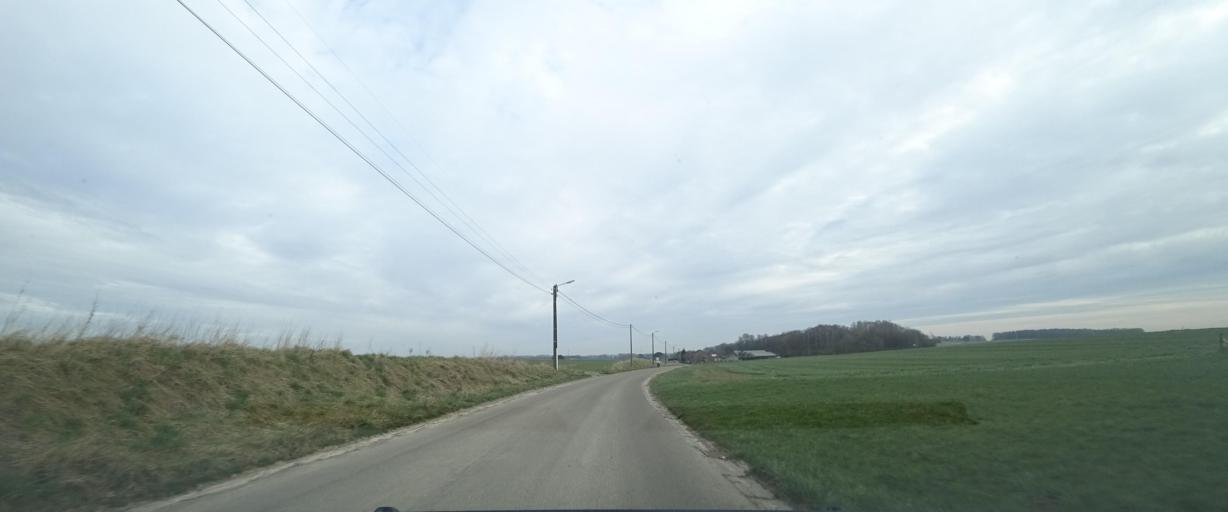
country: BE
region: Wallonia
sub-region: Province de Namur
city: Sombreffe
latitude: 50.4740
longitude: 4.6225
